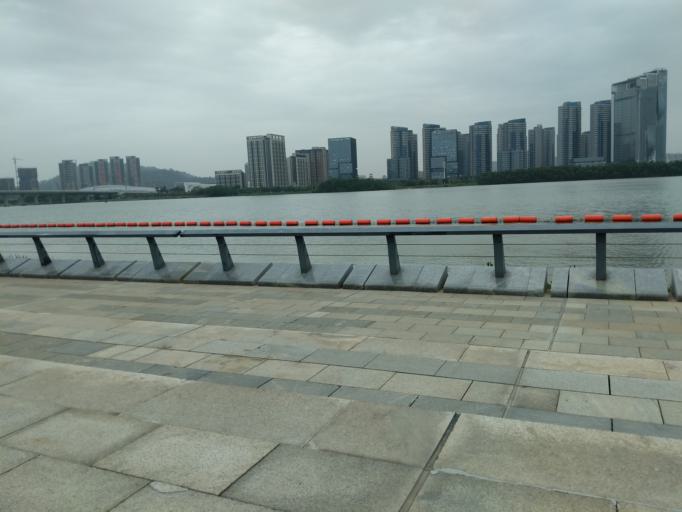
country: CN
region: Guangdong
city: Hengli
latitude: 22.7744
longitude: 113.5126
